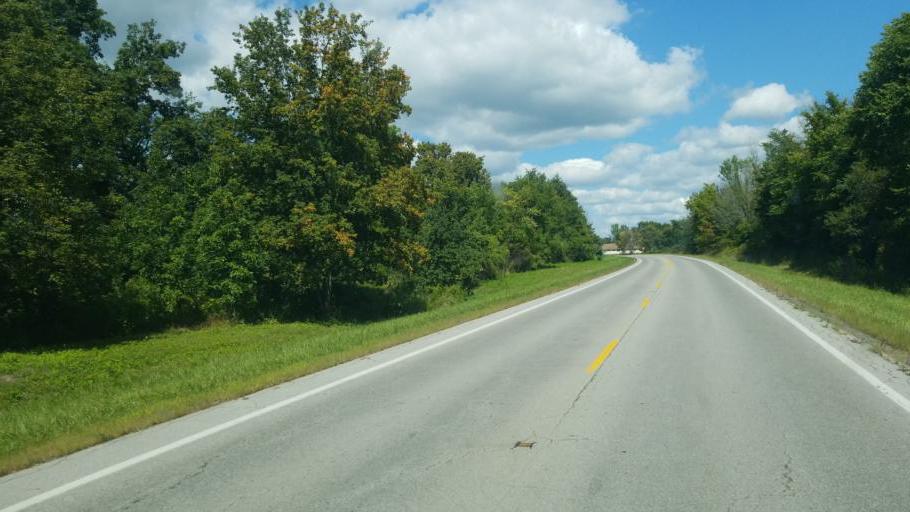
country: US
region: Ohio
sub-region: Ashland County
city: Ashland
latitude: 40.9073
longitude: -82.2826
